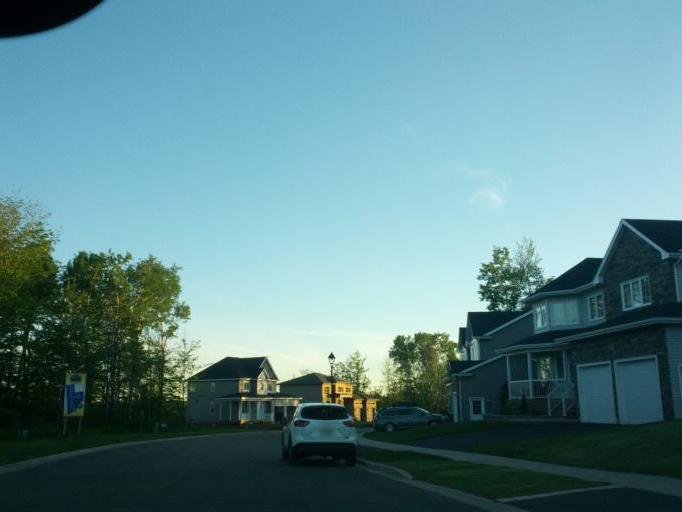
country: CA
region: New Brunswick
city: Moncton
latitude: 46.1123
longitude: -64.8697
